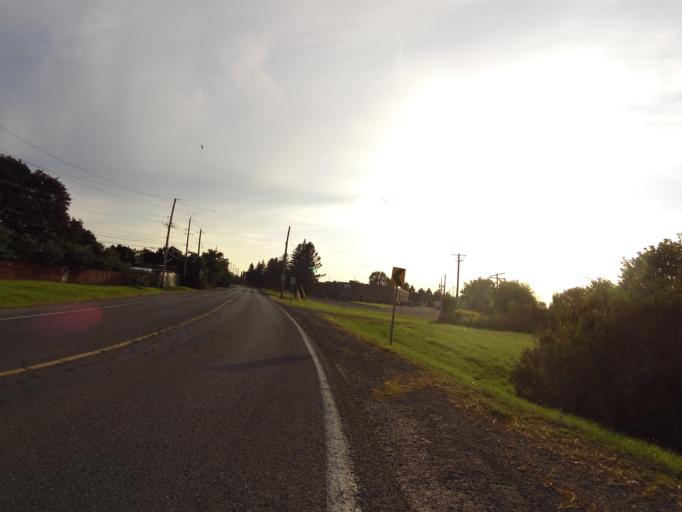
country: CA
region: Ontario
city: Bells Corners
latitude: 45.3311
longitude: -75.8112
